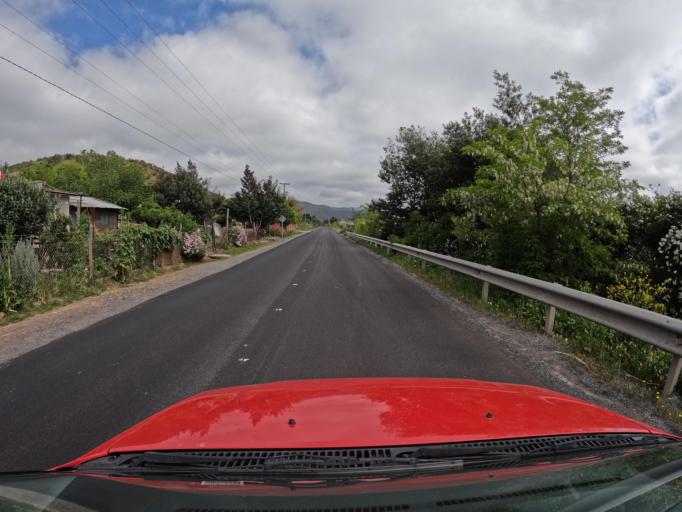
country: CL
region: O'Higgins
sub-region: Provincia de Colchagua
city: Santa Cruz
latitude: -34.6622
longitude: -71.4001
